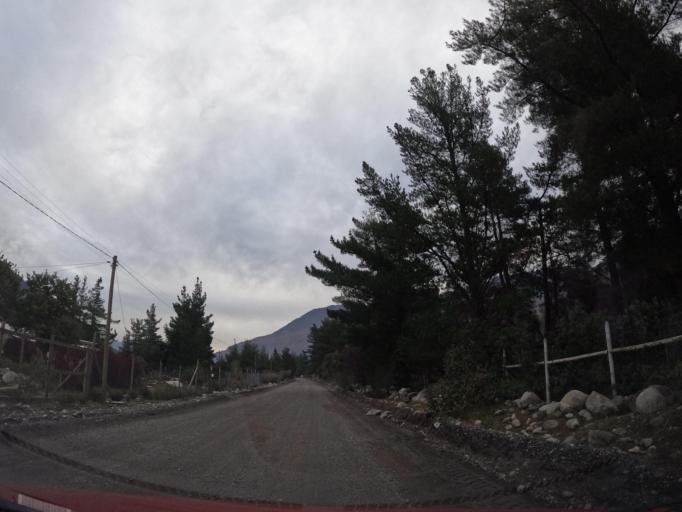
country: CL
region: Maule
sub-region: Provincia de Linares
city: Colbun
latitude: -35.7044
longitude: -71.0840
